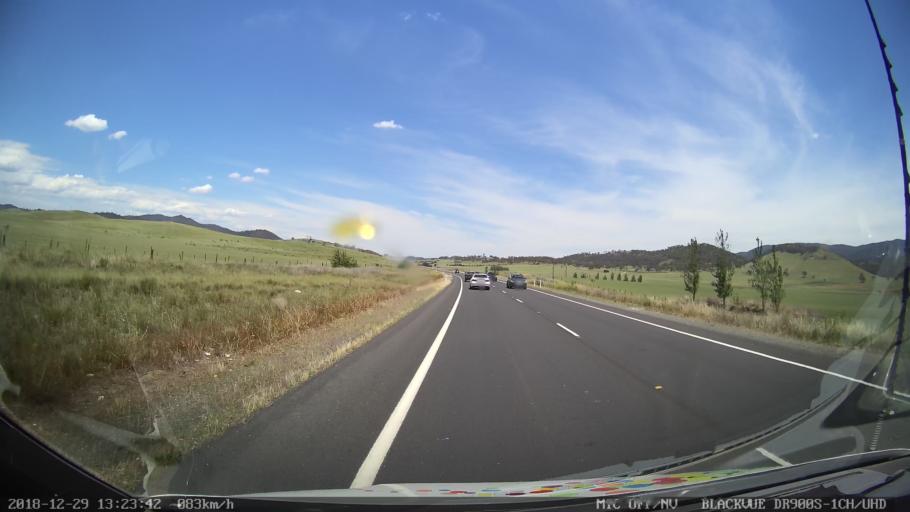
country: AU
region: Australian Capital Territory
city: Macarthur
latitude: -35.8202
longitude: 149.1634
